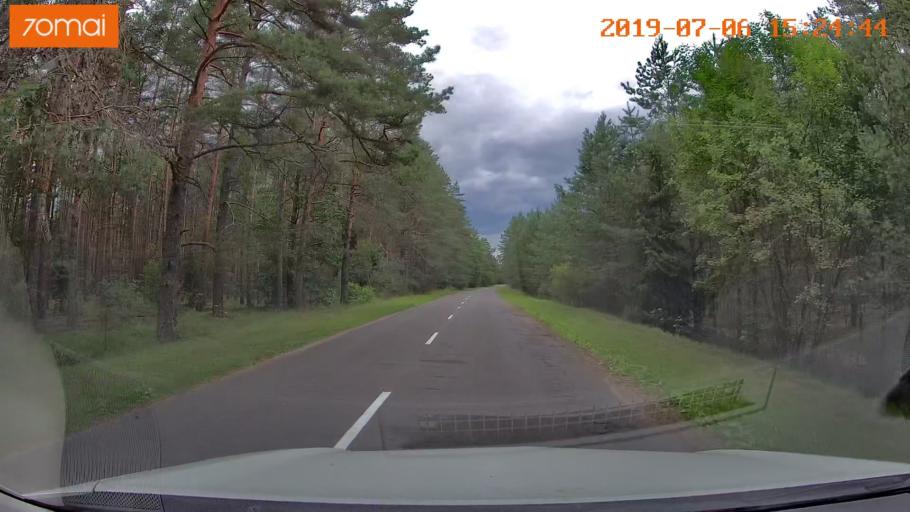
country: BY
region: Minsk
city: Valozhyn
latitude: 54.0229
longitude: 26.6035
